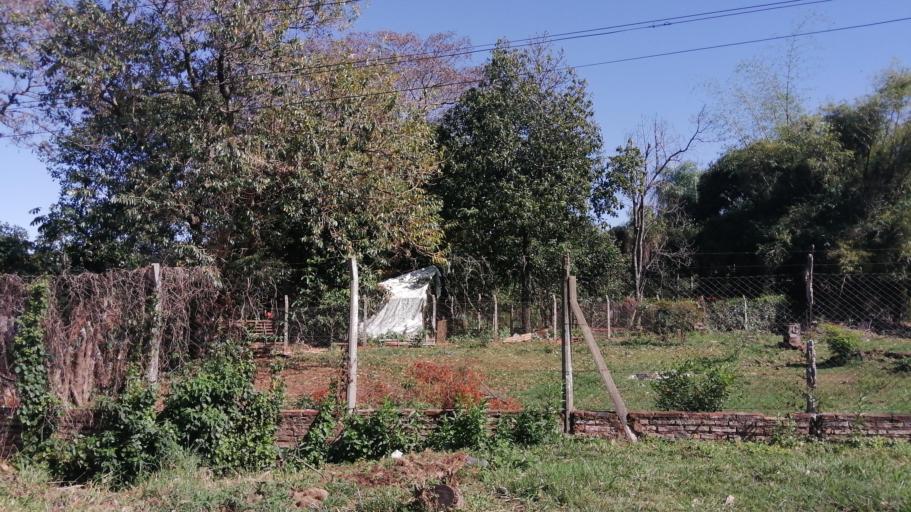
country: PY
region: Misiones
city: San Juan Bautista
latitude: -26.6768
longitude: -57.1437
